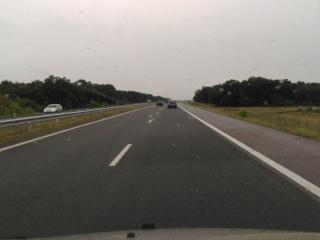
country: BG
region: Stara Zagora
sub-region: Obshtina Stara Zagora
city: Stara Zagora
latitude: 42.3614
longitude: 25.7606
